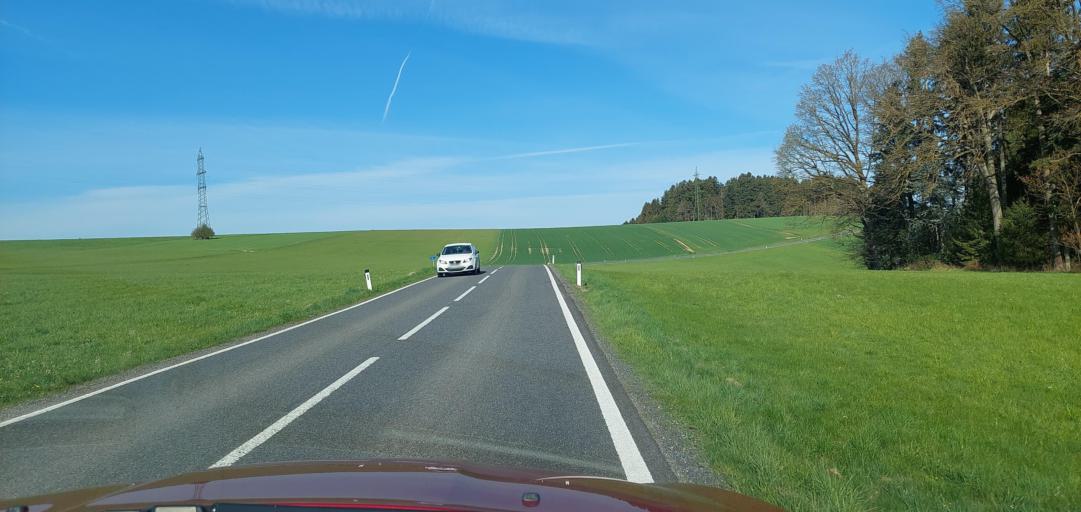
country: AT
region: Upper Austria
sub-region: Politischer Bezirk Ried im Innkreis
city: Ried im Innkreis
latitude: 48.1763
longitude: 13.5378
